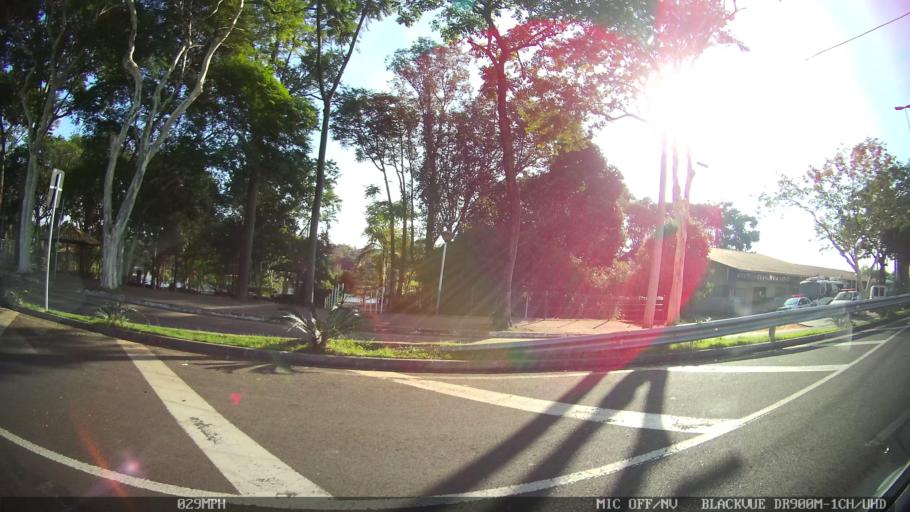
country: BR
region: Sao Paulo
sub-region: Sao Jose Do Rio Preto
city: Sao Jose do Rio Preto
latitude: -20.8108
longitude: -49.3576
